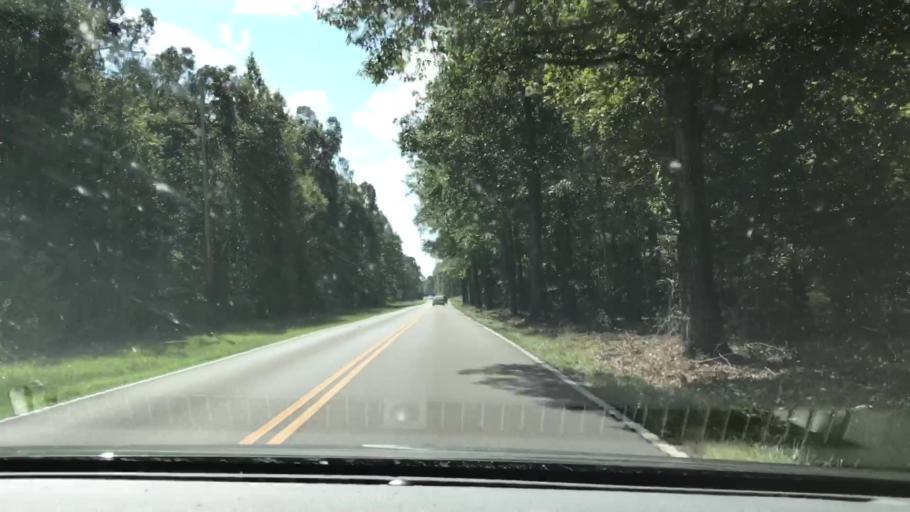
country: US
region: Kentucky
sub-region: McCracken County
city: Reidland
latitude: 36.9624
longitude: -88.5134
